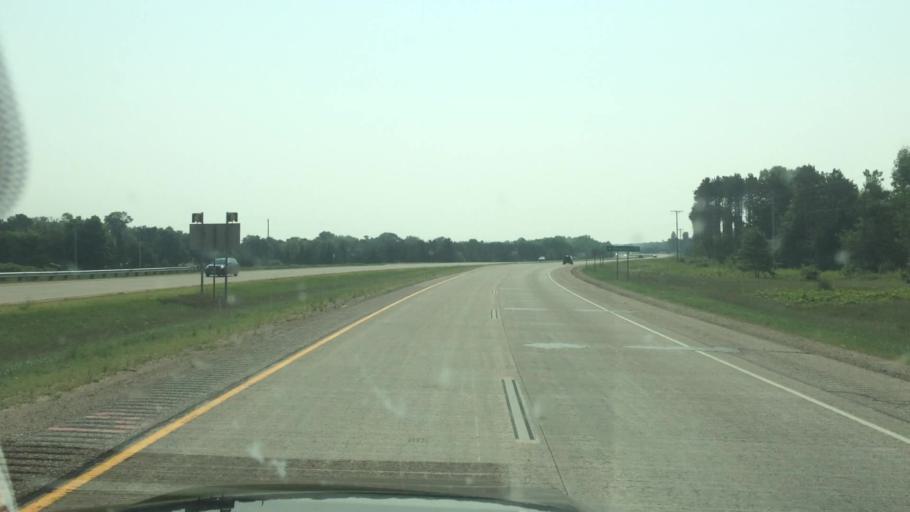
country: US
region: Wisconsin
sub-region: Waupaca County
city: Weyauwega
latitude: 44.3286
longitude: -88.9993
